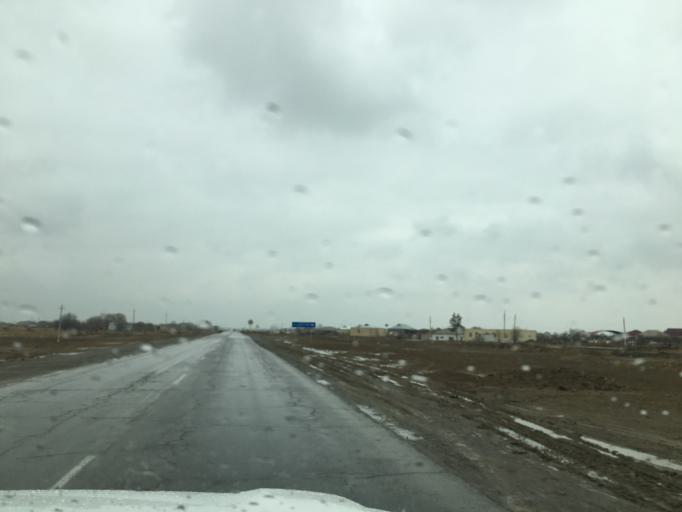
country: TM
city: Murgab
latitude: 37.4685
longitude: 62.0335
